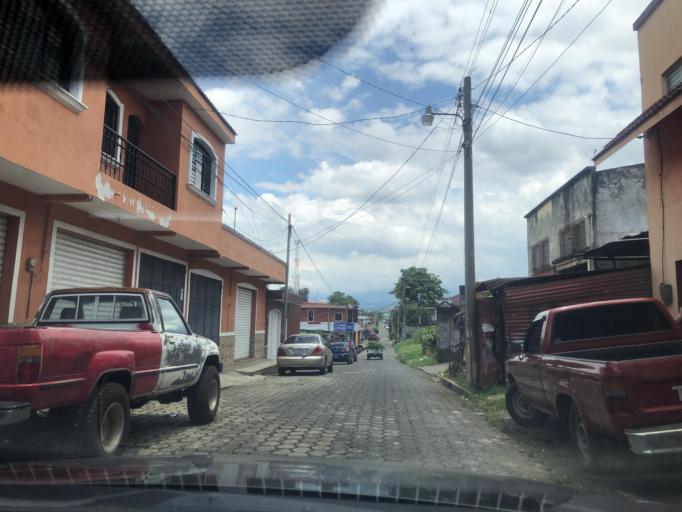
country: GT
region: Quetzaltenango
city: Coatepeque
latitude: 14.7069
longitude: -91.8679
